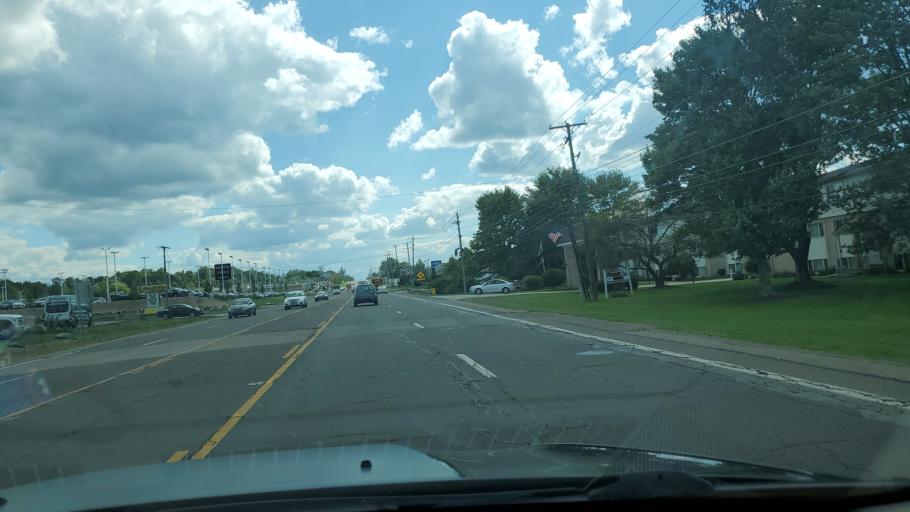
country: US
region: Ohio
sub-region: Mahoning County
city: Boardman
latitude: 41.0078
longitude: -80.6628
